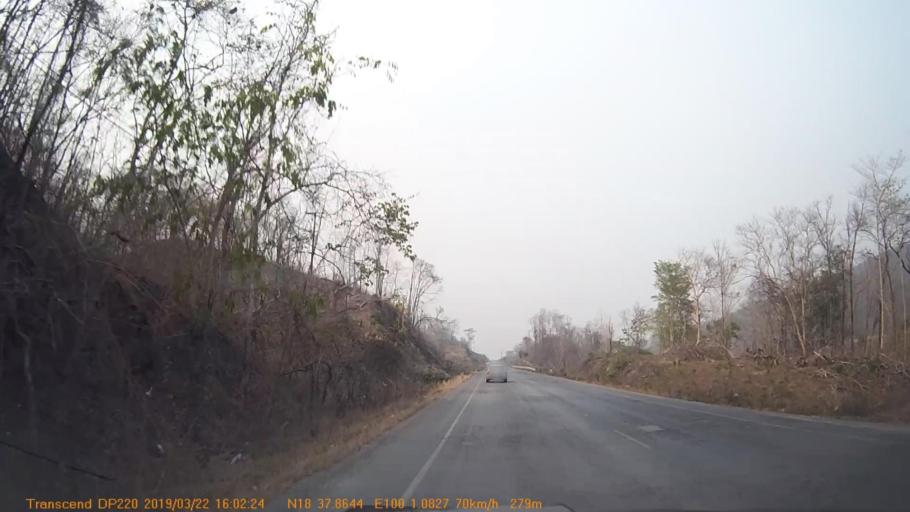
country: TH
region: Lampang
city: Ngao
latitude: 18.6313
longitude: 100.0180
